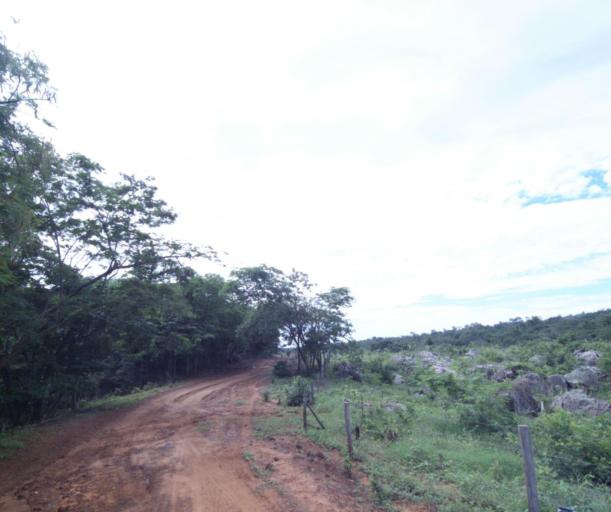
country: BR
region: Bahia
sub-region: Carinhanha
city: Carinhanha
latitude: -14.2156
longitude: -44.4455
